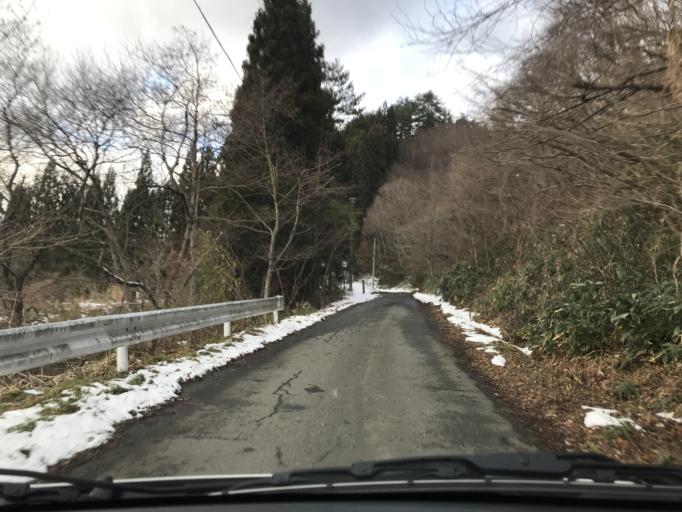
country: JP
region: Iwate
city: Ichinoseki
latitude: 39.0155
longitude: 140.9743
